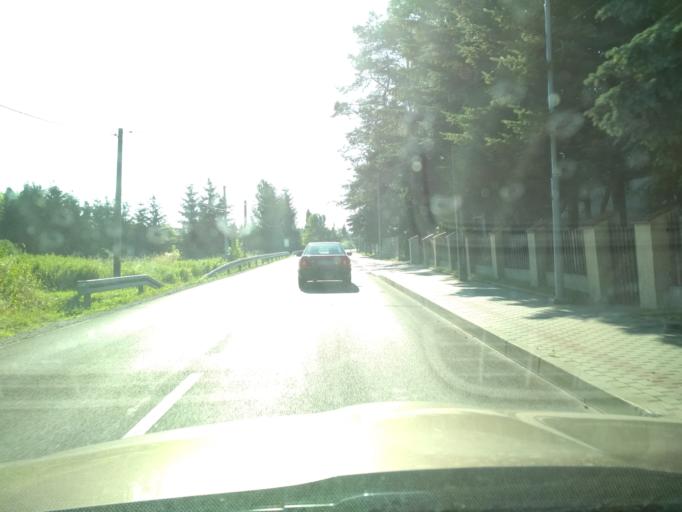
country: PL
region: Subcarpathian Voivodeship
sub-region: Rzeszow
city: Rzeszow
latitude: 50.0632
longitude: 21.9875
